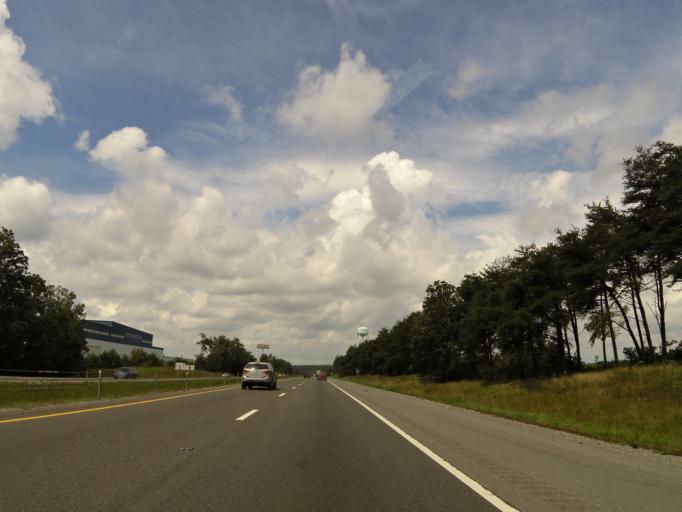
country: US
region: Tennessee
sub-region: Cumberland County
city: Crossville
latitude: 36.0038
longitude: -85.0510
